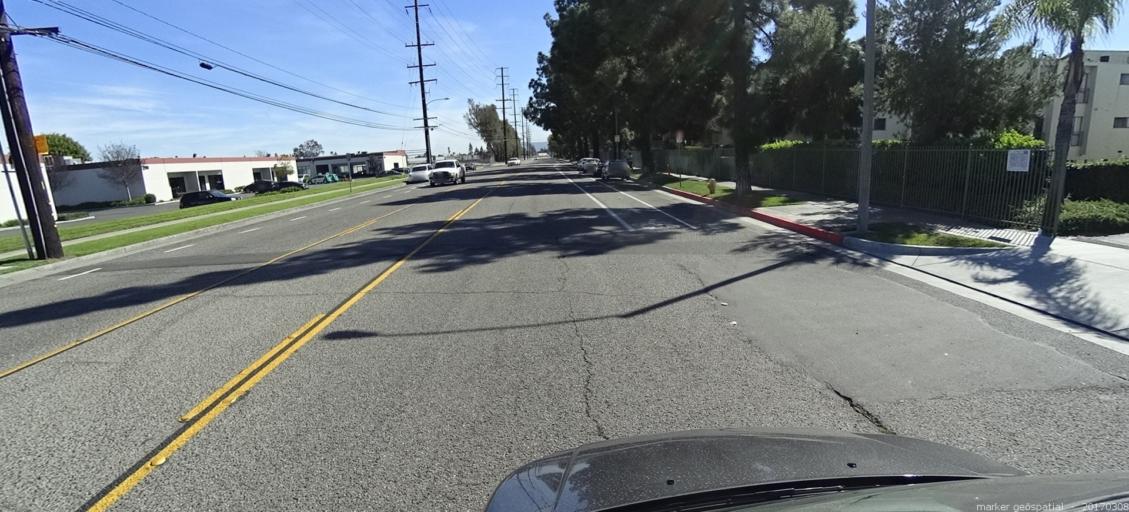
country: US
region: California
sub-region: Orange County
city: Anaheim
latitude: 33.8398
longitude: -117.9562
